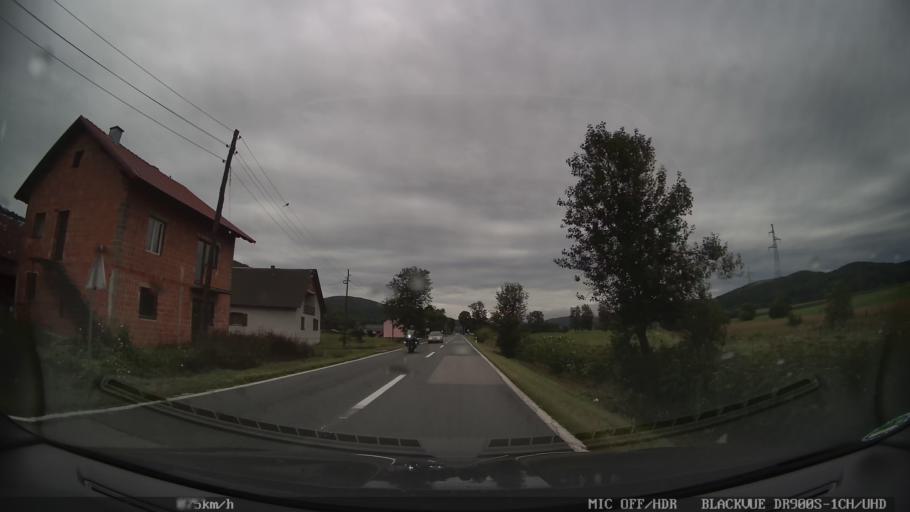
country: HR
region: Licko-Senjska
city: Brinje
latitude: 44.9180
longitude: 15.1528
